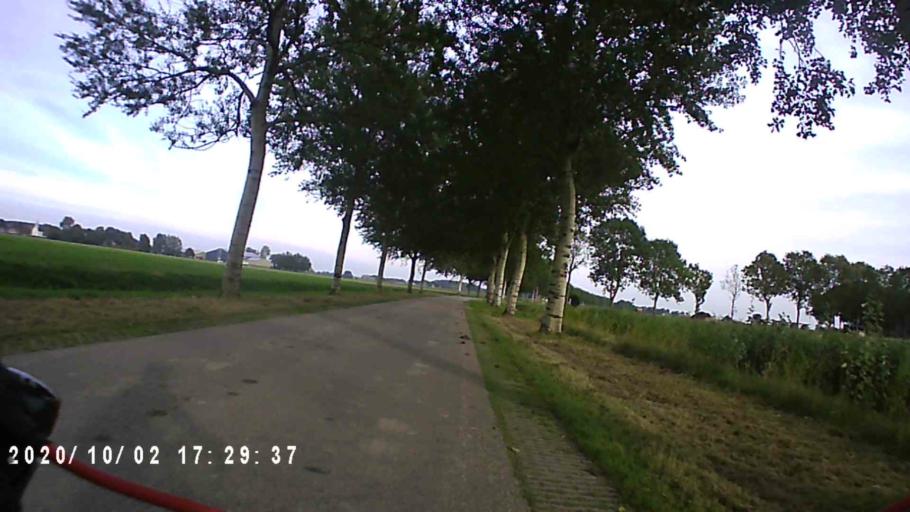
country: NL
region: Groningen
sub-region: Gemeente De Marne
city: Ulrum
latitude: 53.3377
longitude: 6.3219
